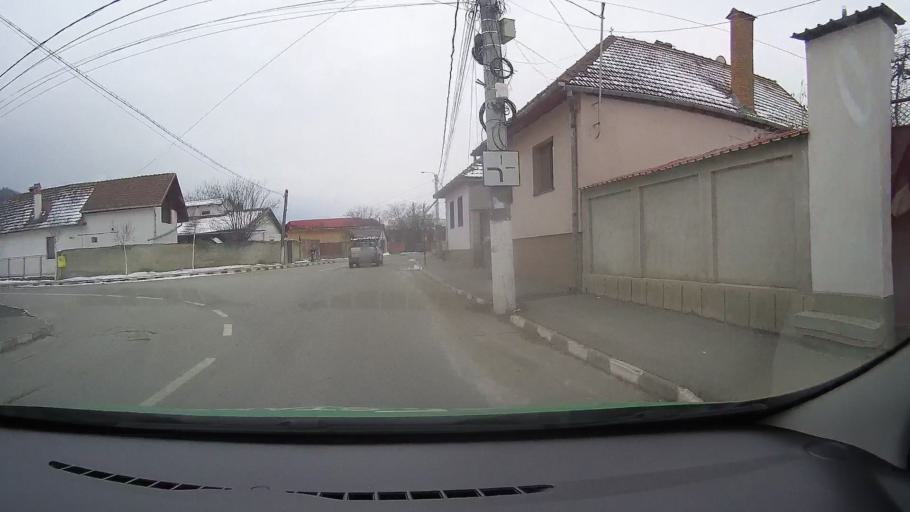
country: RO
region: Brasov
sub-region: Oras Rasnov
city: Rasnov
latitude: 45.5779
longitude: 25.4564
